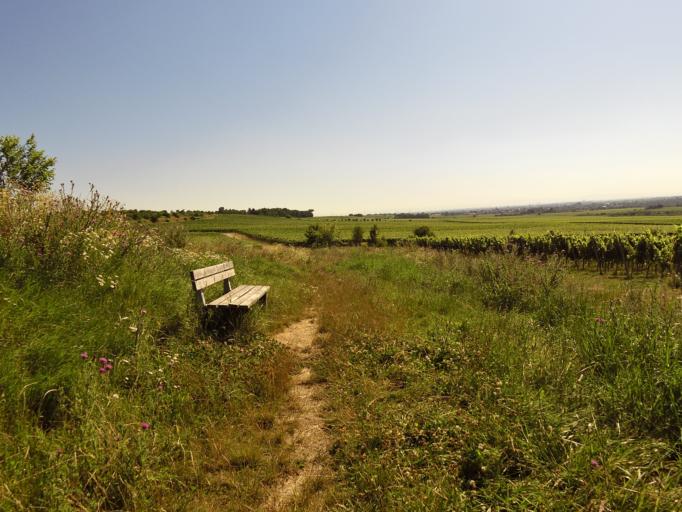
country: DE
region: Rheinland-Pfalz
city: Bissersheim
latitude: 49.5217
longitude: 8.2080
